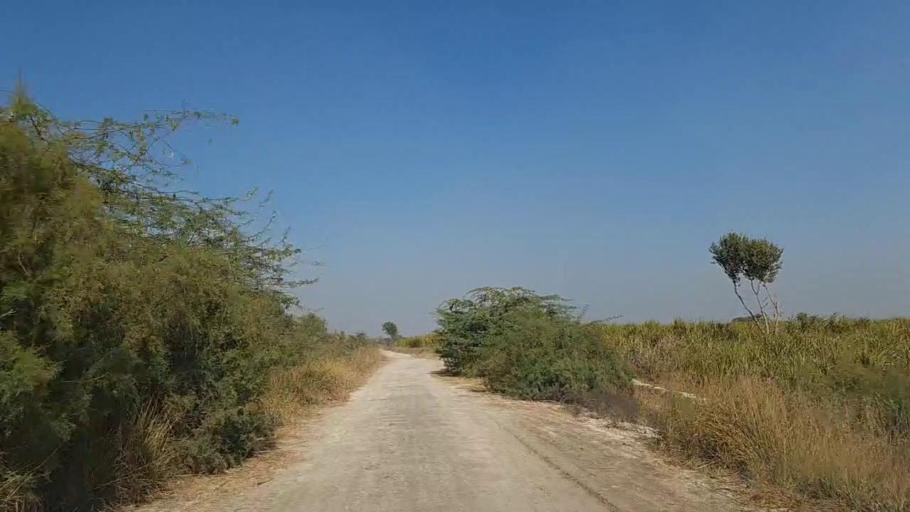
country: PK
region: Sindh
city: Daur
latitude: 26.4930
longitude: 68.3386
